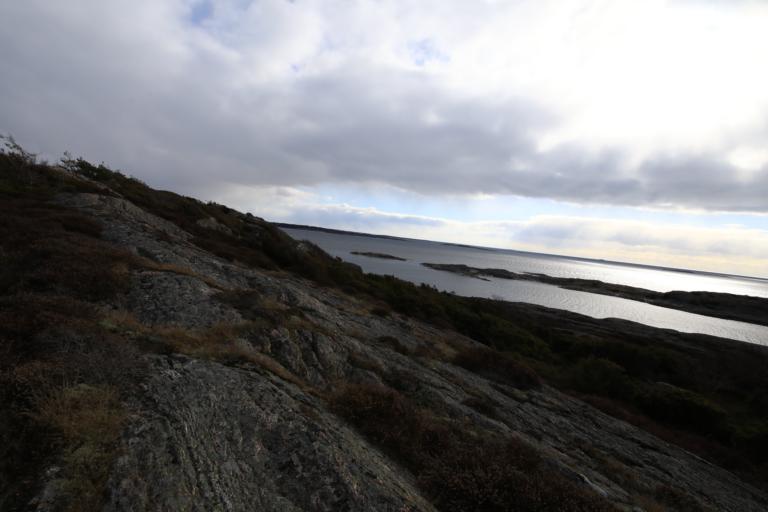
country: SE
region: Halland
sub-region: Kungsbacka Kommun
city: Frillesas
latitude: 57.2153
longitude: 12.1409
